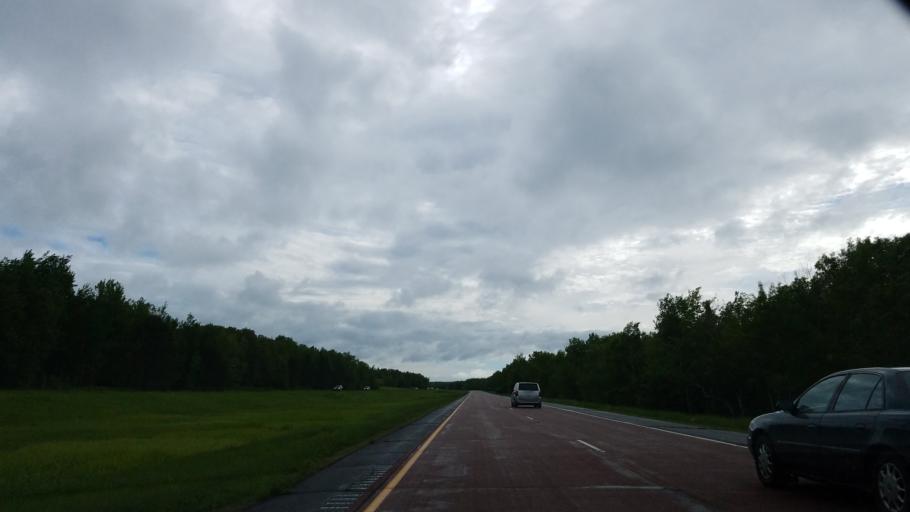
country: US
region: Minnesota
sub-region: Saint Louis County
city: Arnold
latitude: 46.8628
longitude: -91.9704
